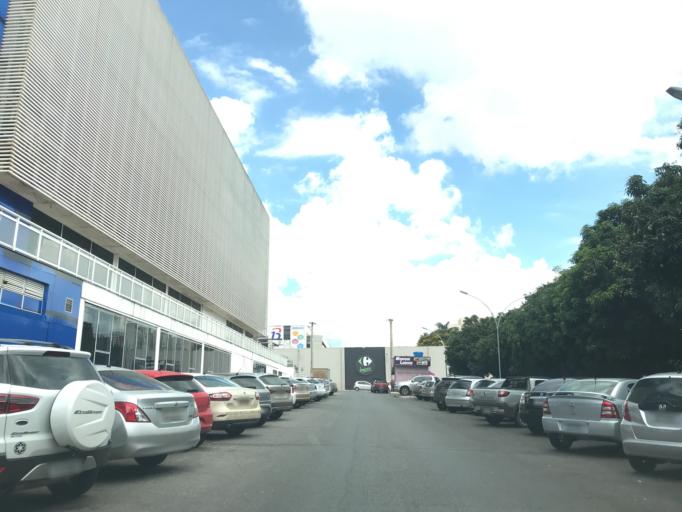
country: BR
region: Federal District
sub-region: Brasilia
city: Brasilia
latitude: -15.7518
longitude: -47.8942
